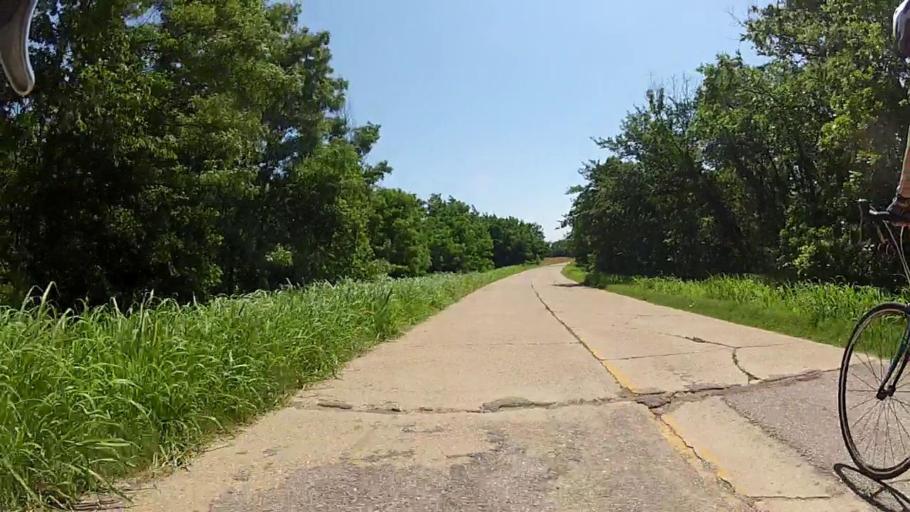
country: US
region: Kansas
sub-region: Sumner County
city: Caldwell
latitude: 37.0341
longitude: -97.4905
